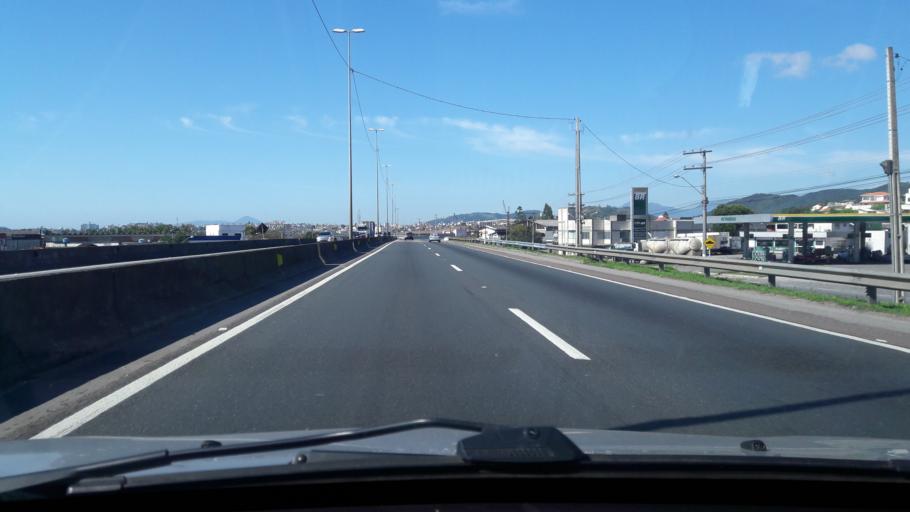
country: BR
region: Santa Catarina
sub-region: Biguacu
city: Biguacu
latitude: -27.5201
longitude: -48.6376
